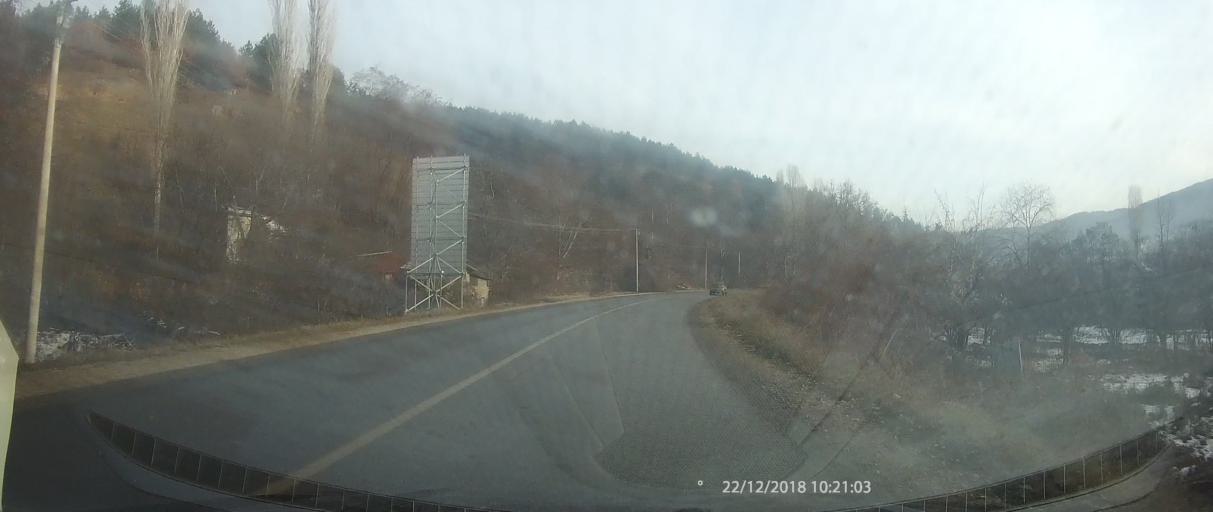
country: MK
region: Kriva Palanka
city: Kriva Palanka
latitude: 42.1965
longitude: 22.3108
